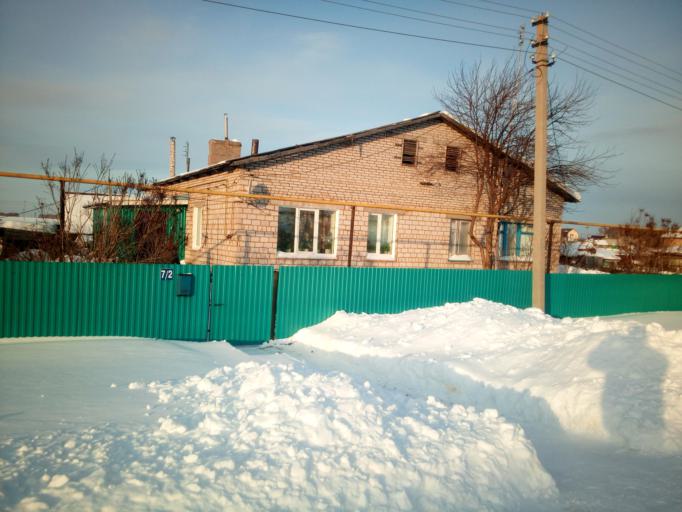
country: RU
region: Bashkortostan
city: Amzya
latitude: 56.1661
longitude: 54.3788
